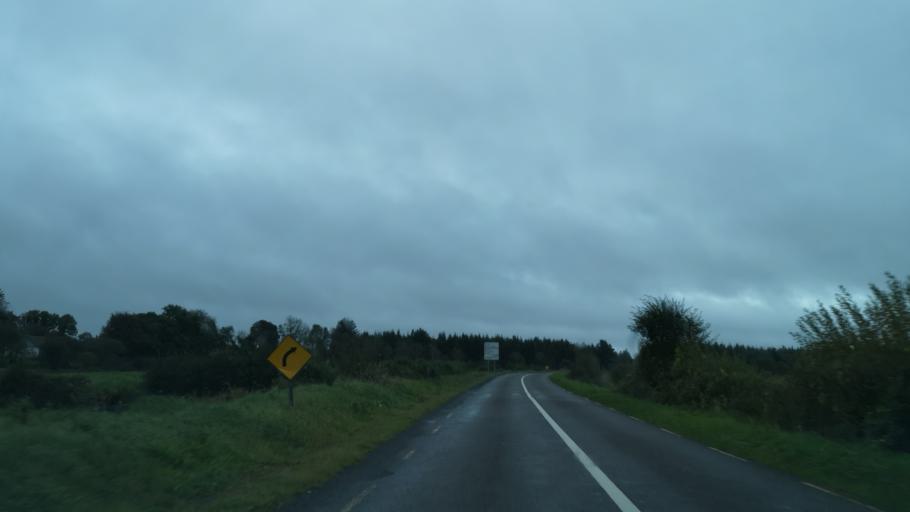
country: IE
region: Connaught
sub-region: Maigh Eo
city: Ballyhaunis
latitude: 53.8106
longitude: -8.6679
